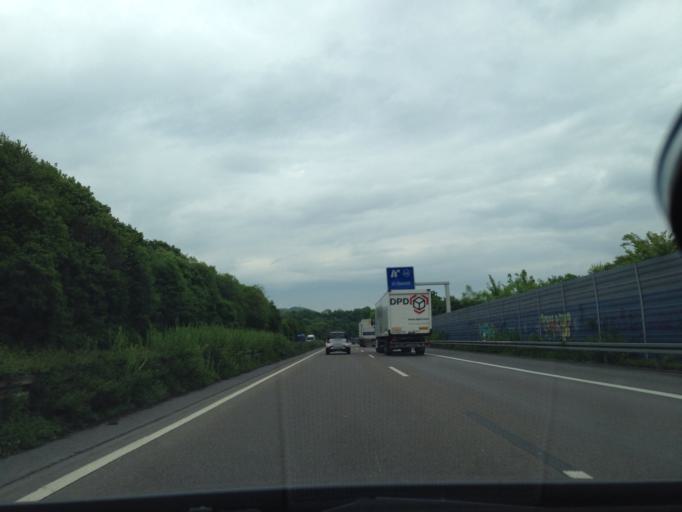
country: DE
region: North Rhine-Westphalia
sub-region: Regierungsbezirk Arnsberg
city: Nachrodt-Wiblingwerde
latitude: 51.3714
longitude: 7.6047
